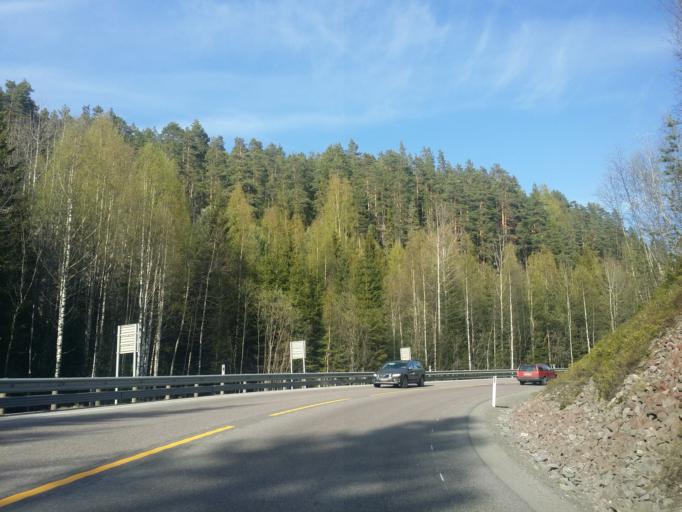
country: NO
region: Telemark
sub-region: Notodden
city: Notodden
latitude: 59.5962
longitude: 9.3755
